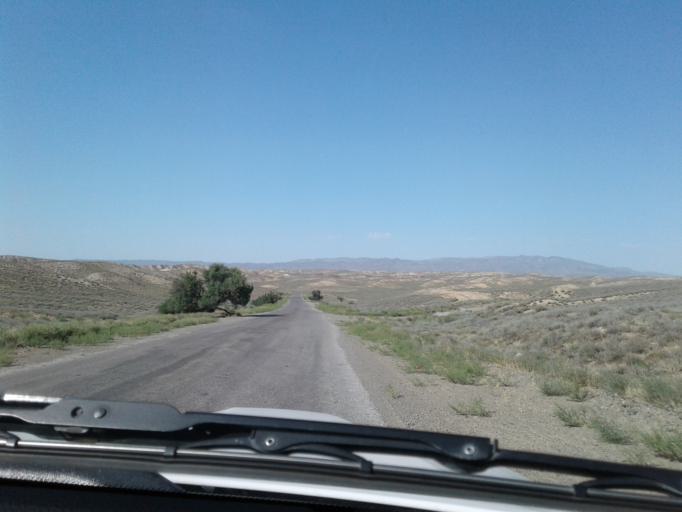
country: TM
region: Balkan
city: Magtymguly
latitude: 38.6565
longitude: 56.2818
